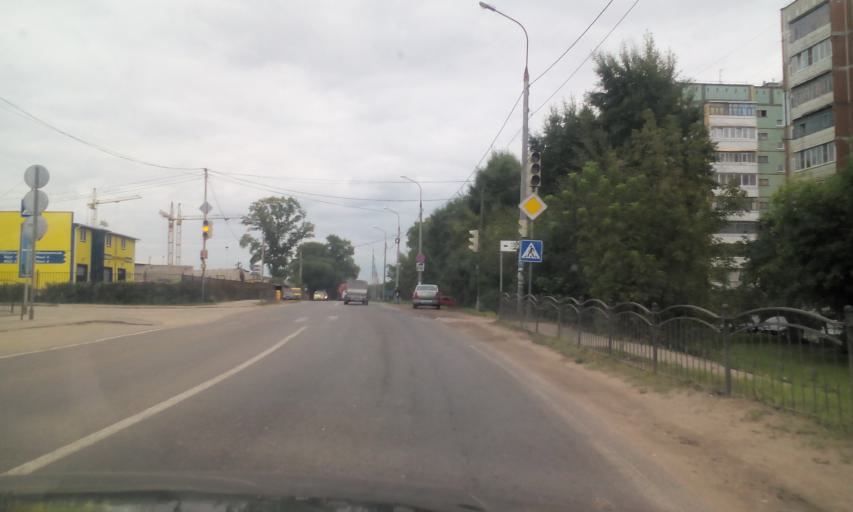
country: RU
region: Kaluga
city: Kaluga
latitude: 54.5148
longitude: 36.3522
